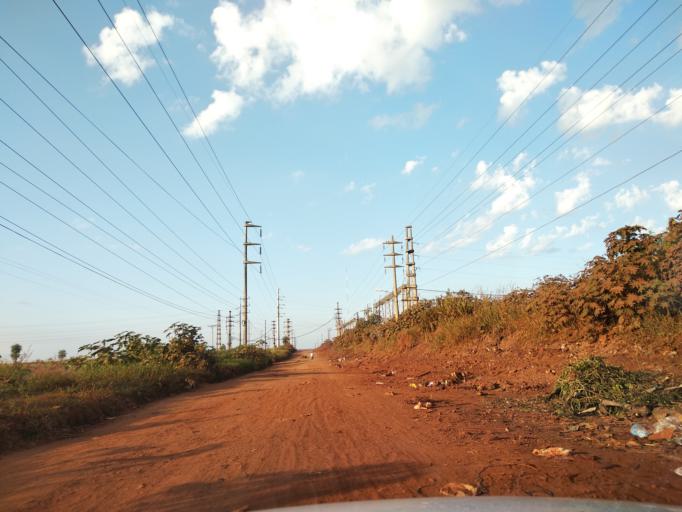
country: AR
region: Misiones
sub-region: Departamento de Capital
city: Posadas
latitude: -27.4405
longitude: -55.9160
